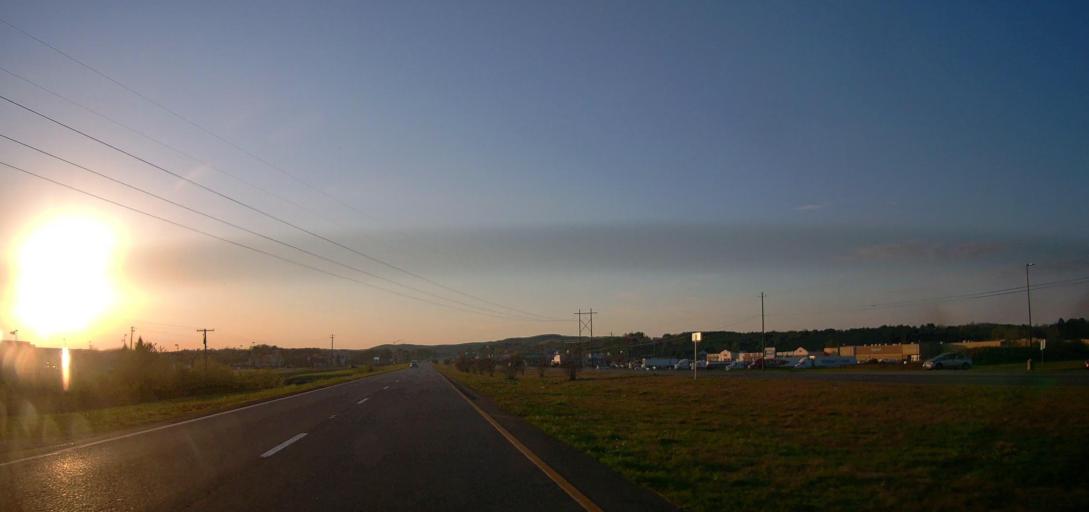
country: US
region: Alabama
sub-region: Talladega County
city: Mignon
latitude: 33.1725
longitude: -86.2847
